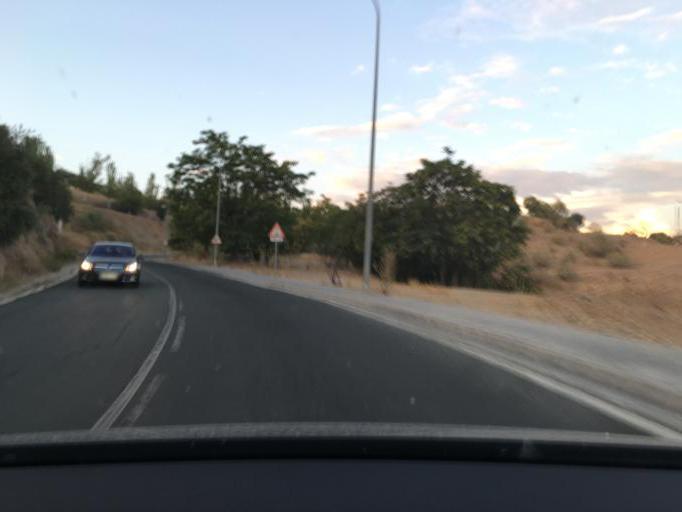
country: ES
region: Andalusia
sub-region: Provincia de Granada
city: Viznar
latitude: 37.2059
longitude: -3.5589
